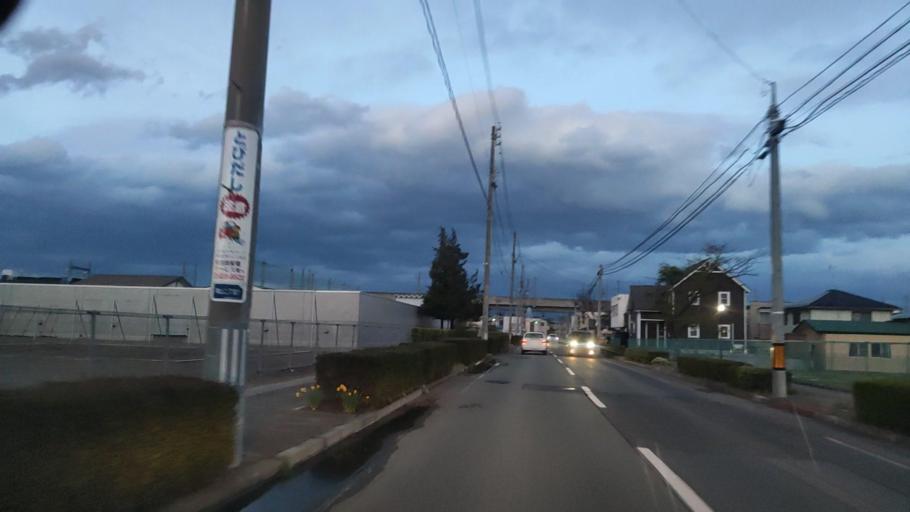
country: JP
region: Iwate
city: Morioka-shi
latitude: 39.7231
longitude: 141.1142
